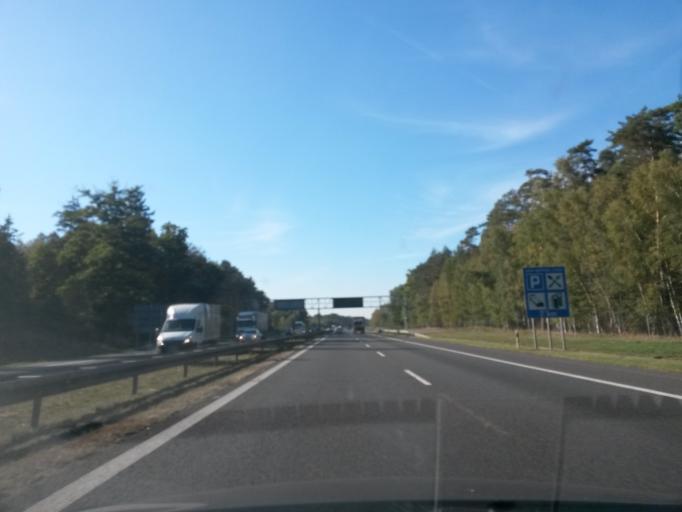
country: PL
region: Opole Voivodeship
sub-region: Powiat opolski
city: Dabrowa
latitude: 50.6648
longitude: 17.6860
